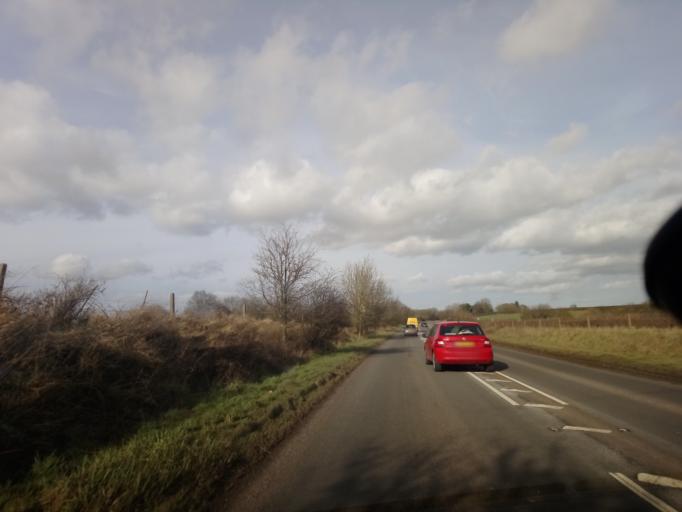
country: GB
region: England
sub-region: Telford and Wrekin
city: Eyton upon the Weald Moors
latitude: 52.7781
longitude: -2.5537
